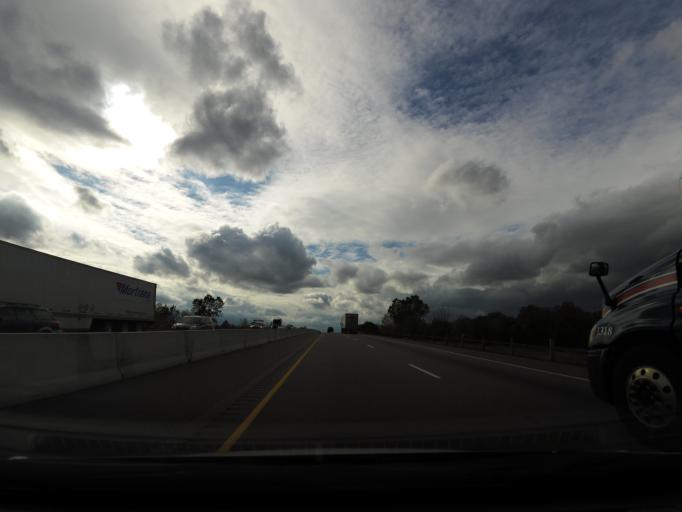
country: CA
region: Ontario
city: Deseronto
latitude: 44.2231
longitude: -77.2189
